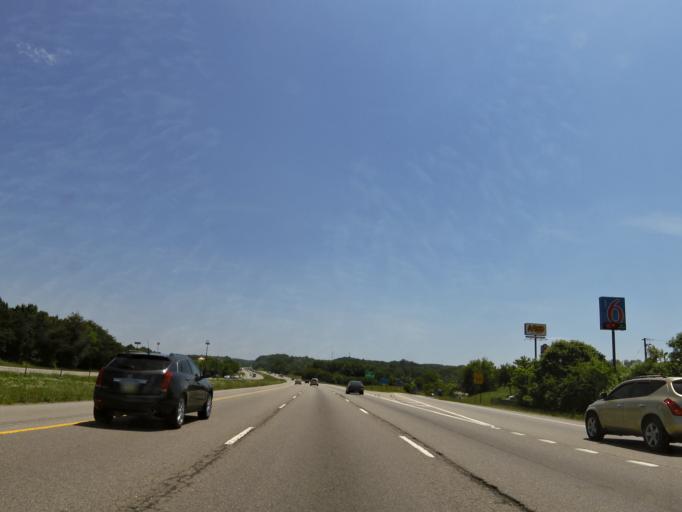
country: US
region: Tennessee
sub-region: Knox County
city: Mascot
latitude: 36.0027
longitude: -83.7802
